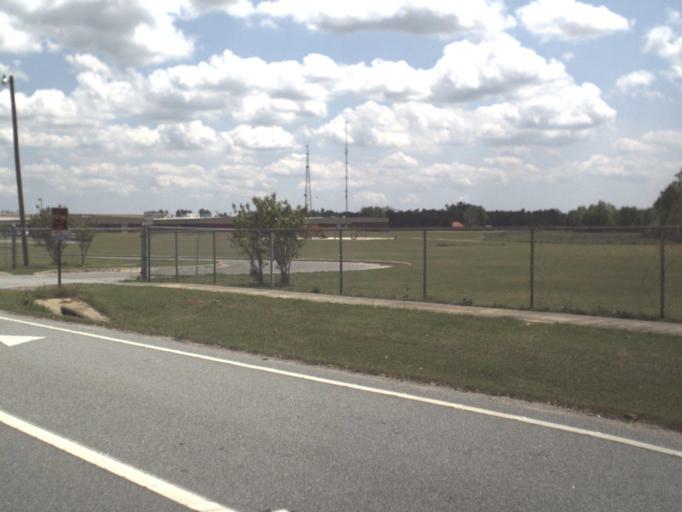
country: US
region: Florida
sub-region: Escambia County
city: Molino
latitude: 30.7432
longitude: -87.3644
